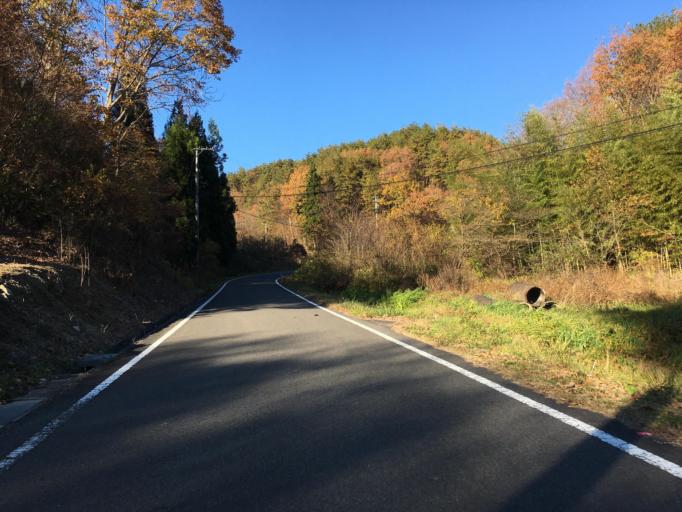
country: JP
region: Fukushima
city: Ishikawa
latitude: 37.2353
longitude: 140.5225
